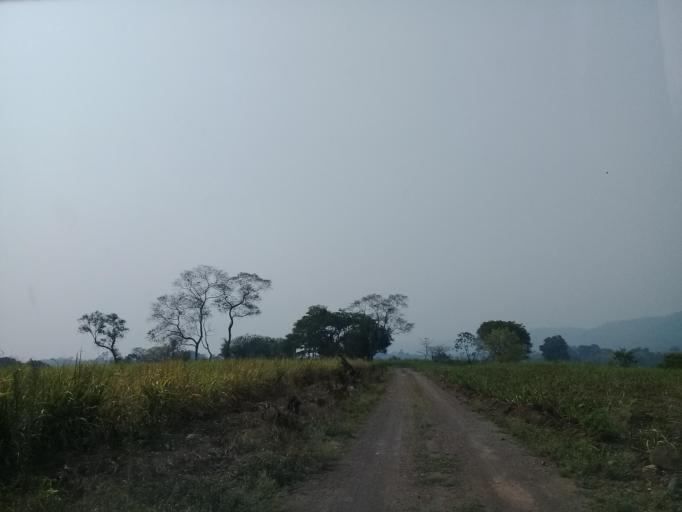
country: MX
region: Oaxaca
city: Acatlan de Perez Figueroa
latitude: 18.6027
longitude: -96.5766
